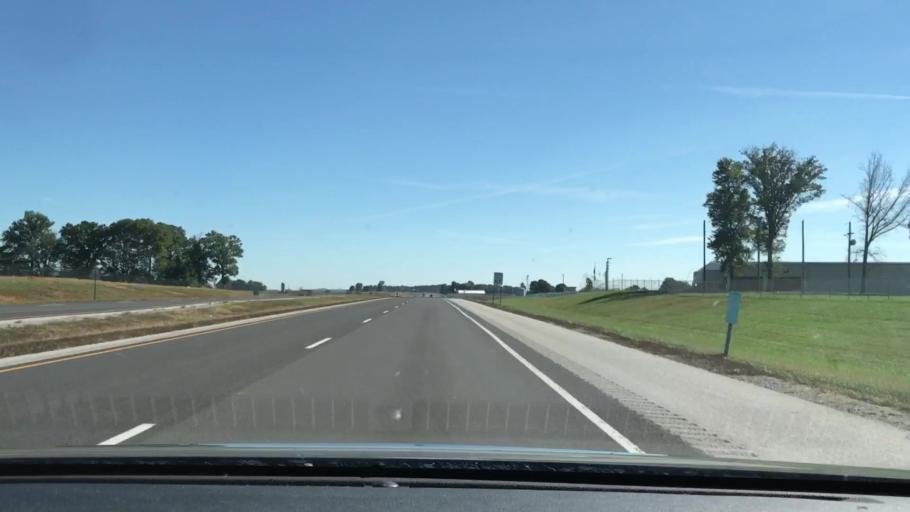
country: US
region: Kentucky
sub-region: Todd County
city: Elkton
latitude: 36.8046
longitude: -87.0661
